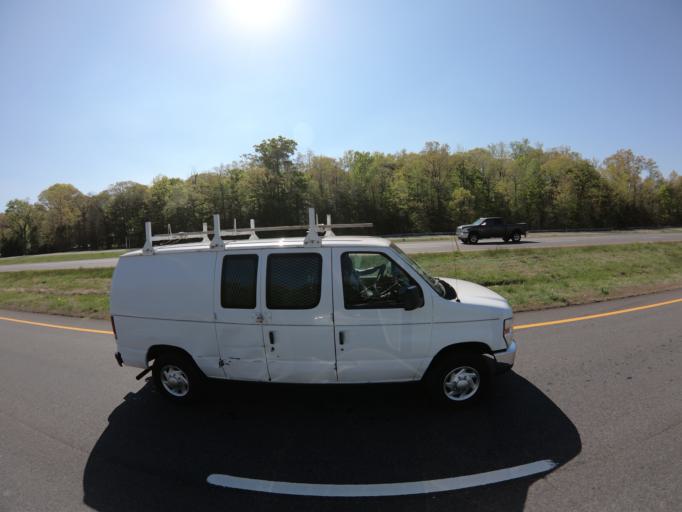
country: US
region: Maryland
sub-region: Prince George's County
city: Accokeek
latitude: 38.6559
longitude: -77.0288
